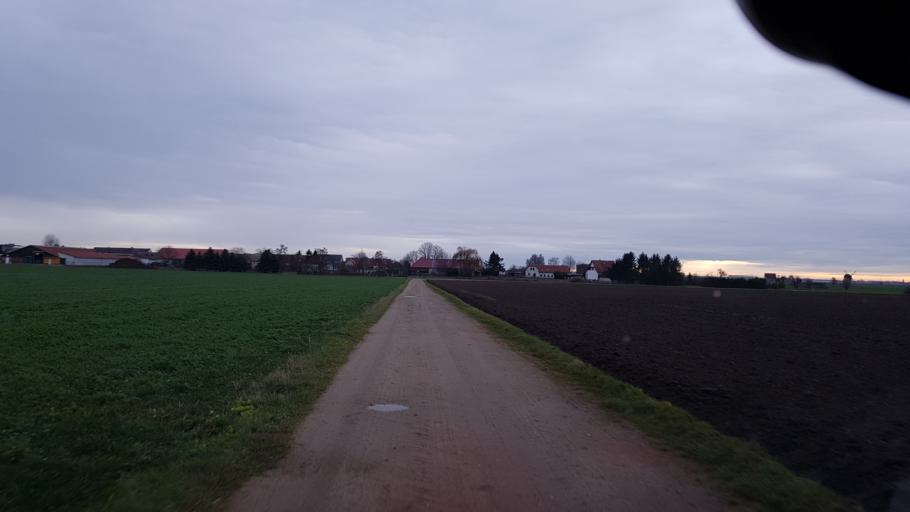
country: DE
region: Brandenburg
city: Doberlug-Kirchhain
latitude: 51.6888
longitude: 13.5051
